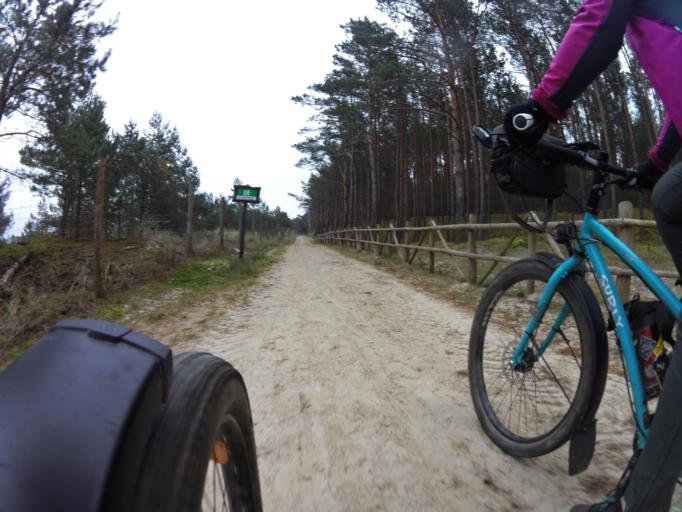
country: PL
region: Pomeranian Voivodeship
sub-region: Powiat pucki
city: Krokowa
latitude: 54.8321
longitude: 18.0964
